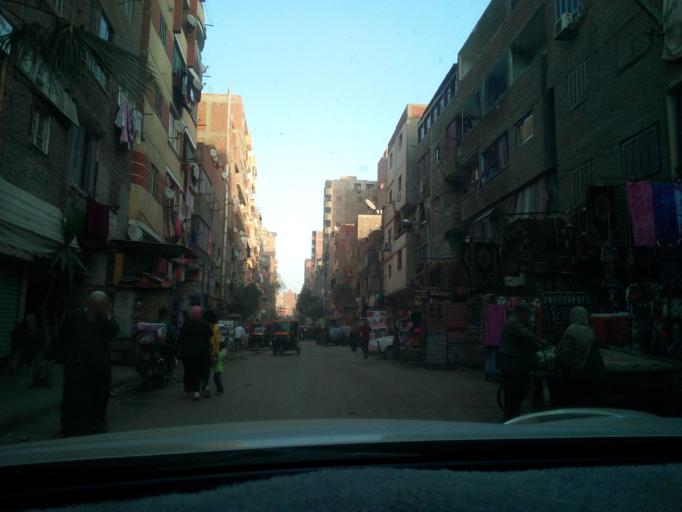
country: EG
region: Muhafazat al Qalyubiyah
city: Al Khankah
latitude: 30.1311
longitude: 31.3412
